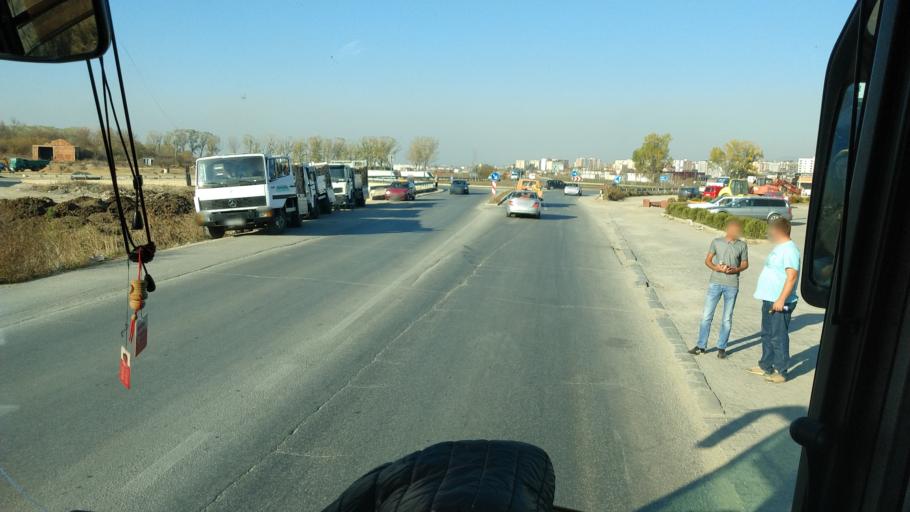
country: XK
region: Pristina
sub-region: Lipjan
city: Lipljan
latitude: 42.5103
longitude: 21.1124
